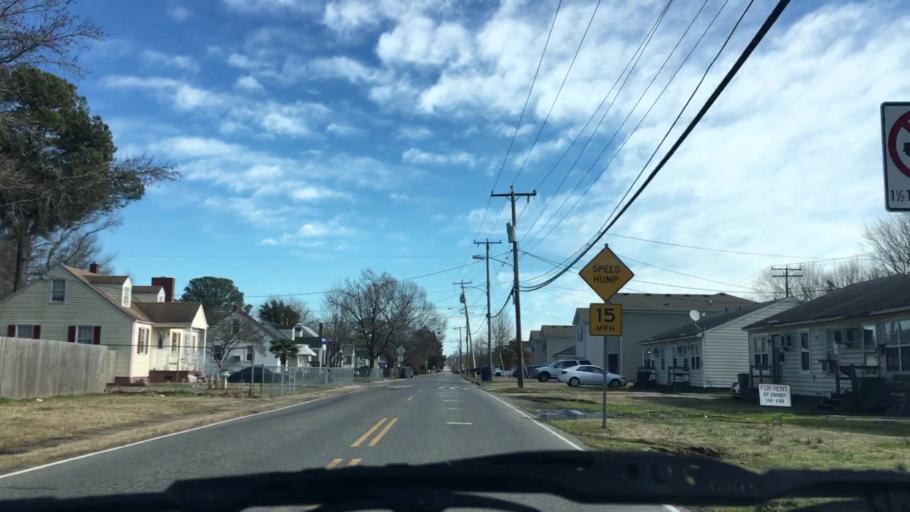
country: US
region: Virginia
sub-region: City of Norfolk
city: Norfolk
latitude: 36.8658
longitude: -76.2435
